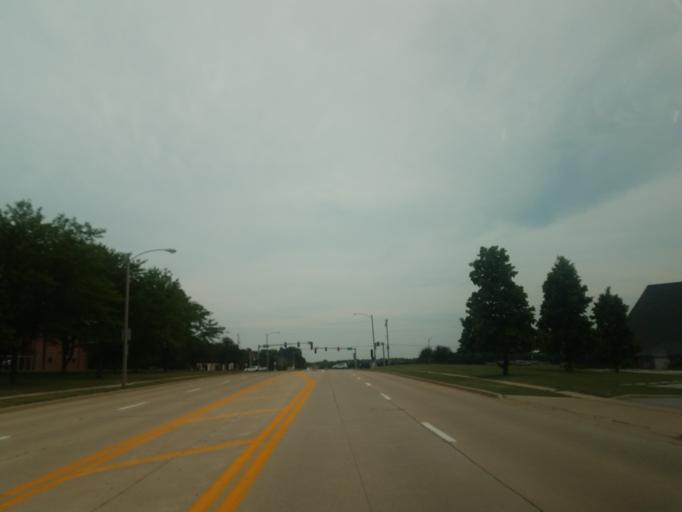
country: US
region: Illinois
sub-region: McLean County
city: Normal
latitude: 40.5118
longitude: -88.9420
